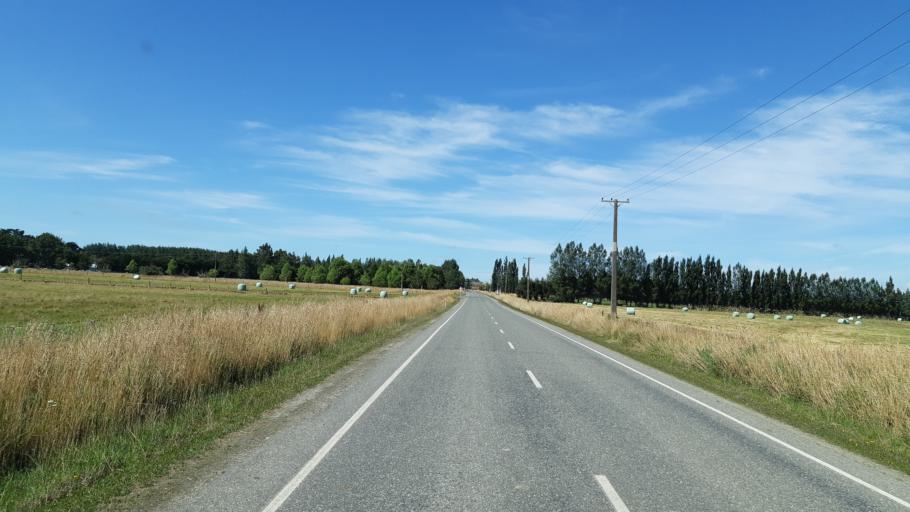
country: NZ
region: Southland
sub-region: Gore District
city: Gore
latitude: -46.0012
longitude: 168.8698
